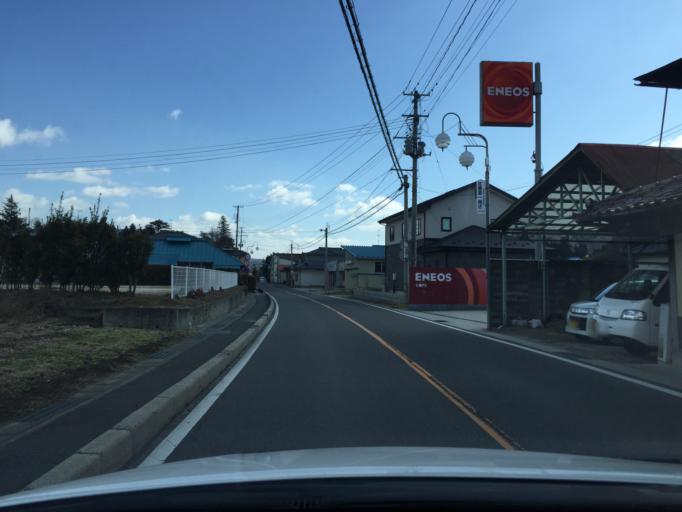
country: JP
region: Fukushima
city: Funehikimachi-funehiki
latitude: 37.3977
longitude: 140.5684
